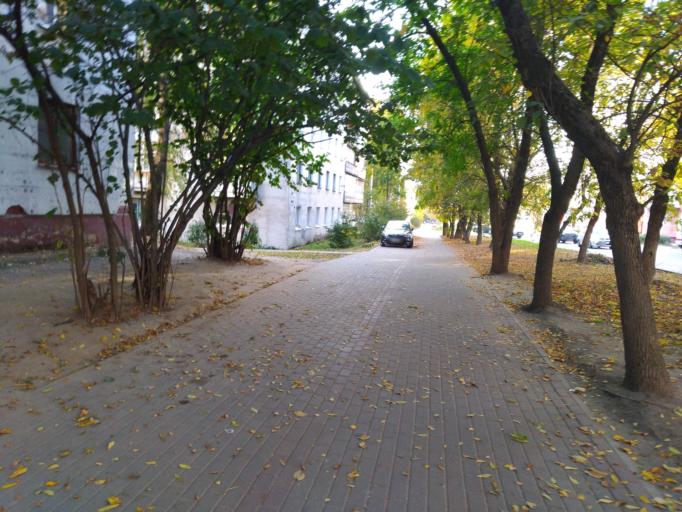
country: RU
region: Kaluga
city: Kaluga
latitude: 54.5219
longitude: 36.2521
